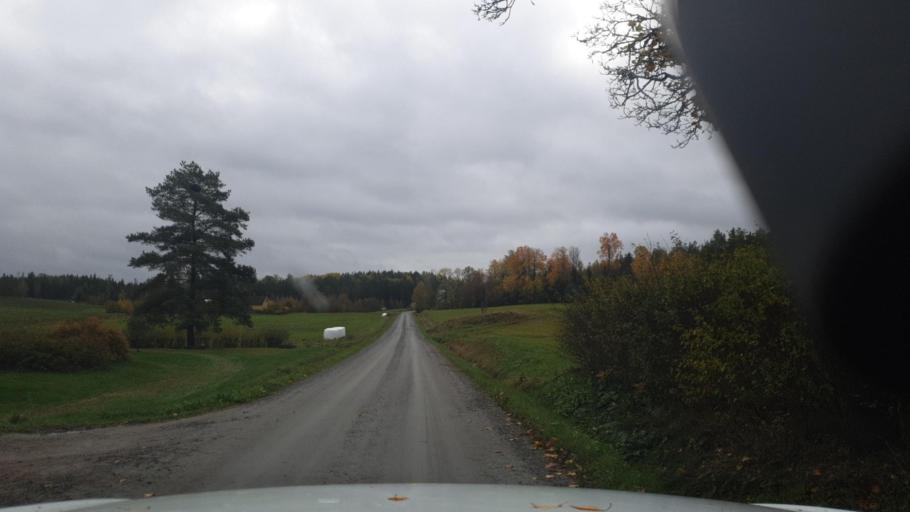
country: SE
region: Vaermland
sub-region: Karlstads Kommun
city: Edsvalla
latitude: 59.5064
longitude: 13.0284
